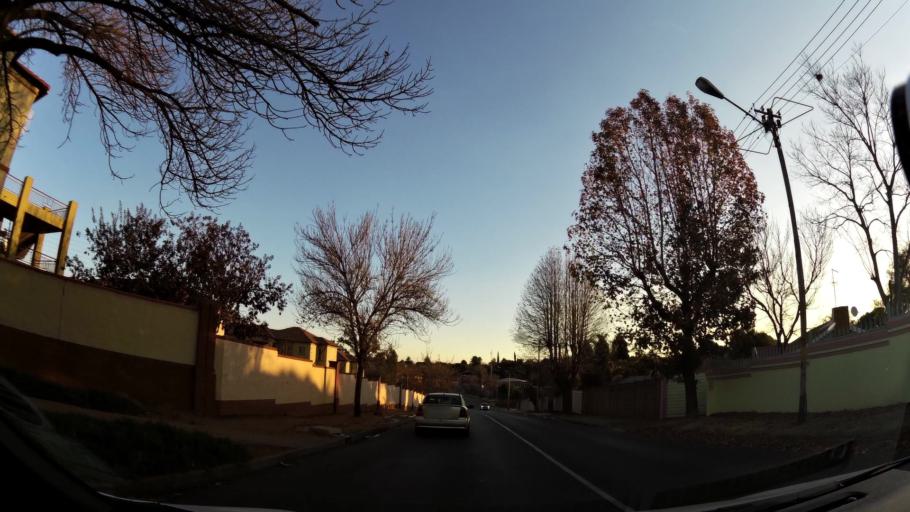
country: ZA
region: Gauteng
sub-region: Ekurhuleni Metropolitan Municipality
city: Germiston
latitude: -26.2561
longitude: 28.1669
